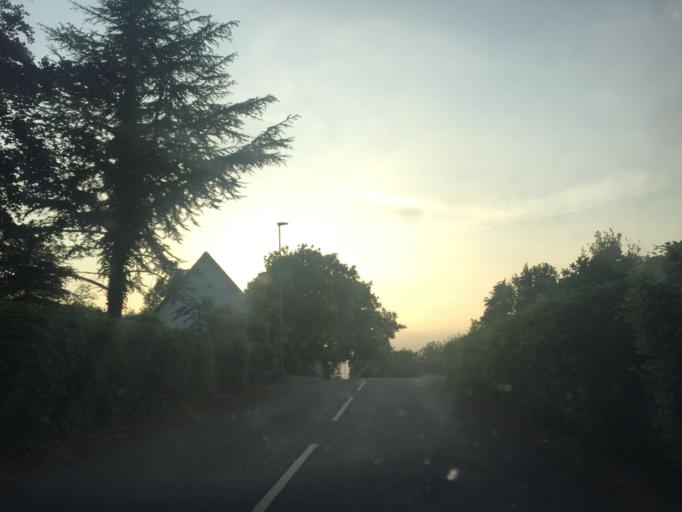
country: DK
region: South Denmark
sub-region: Odense Kommune
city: Bellinge
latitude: 55.3813
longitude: 10.3076
